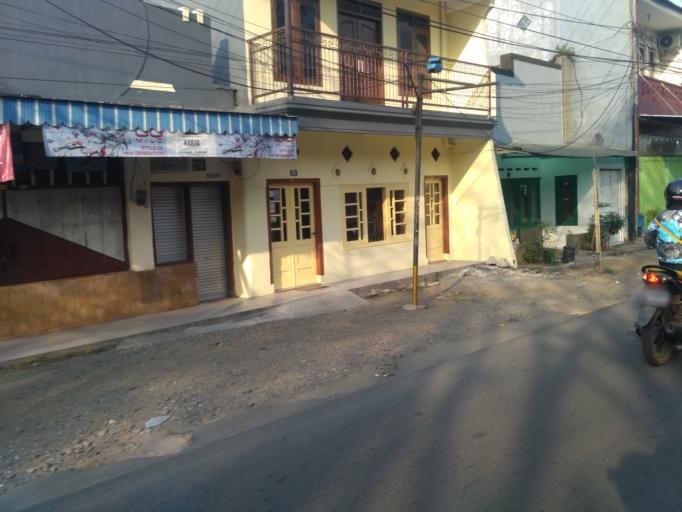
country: ID
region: East Java
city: Malang
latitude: -7.9626
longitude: 112.6264
